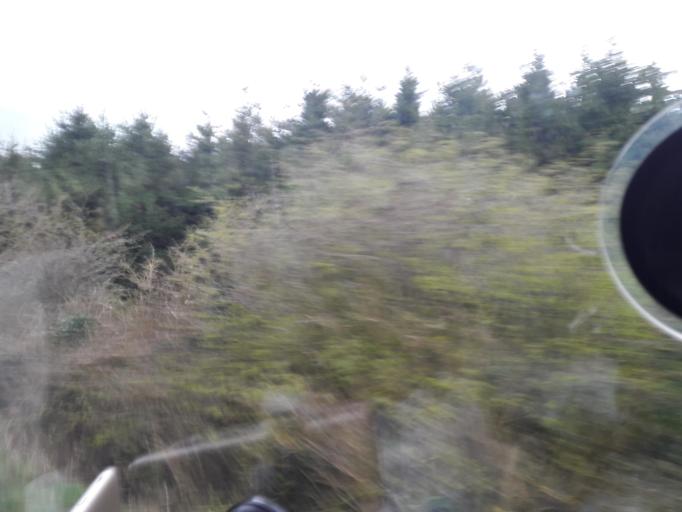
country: IE
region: Leinster
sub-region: An Iarmhi
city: Rathwire
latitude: 53.4903
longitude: -7.2075
